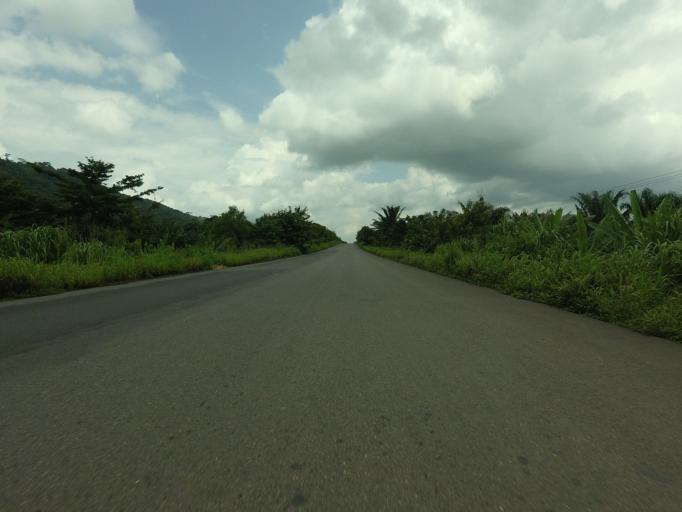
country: GH
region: Volta
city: Ho
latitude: 6.6120
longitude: 0.3009
